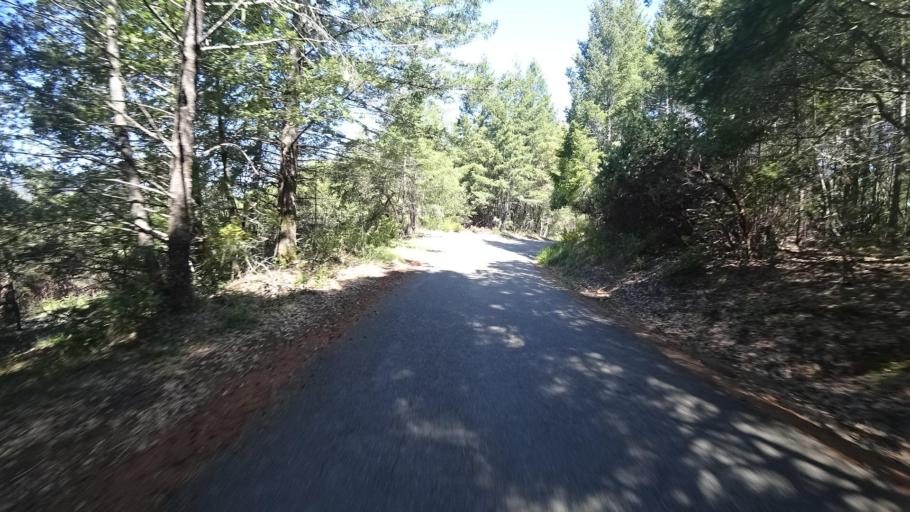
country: US
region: California
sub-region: Humboldt County
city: Redway
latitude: 40.1925
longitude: -124.0944
